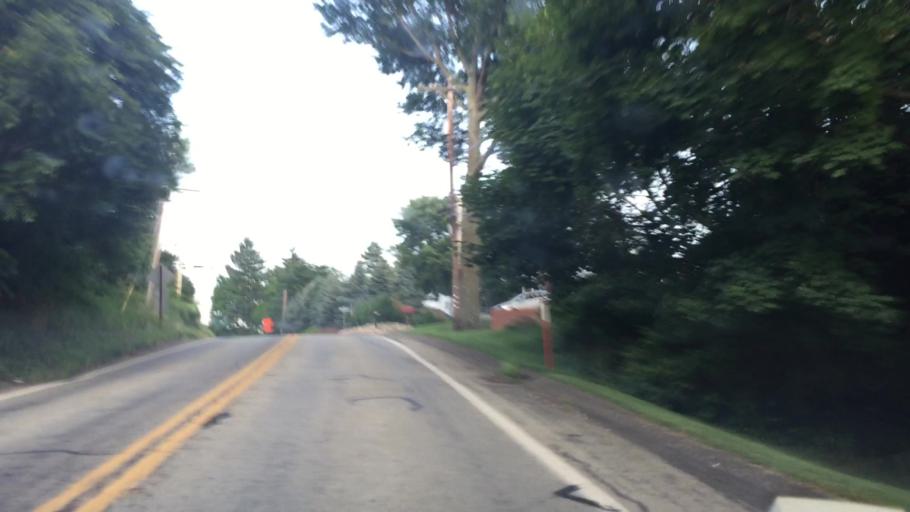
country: US
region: Pennsylvania
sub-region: Allegheny County
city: Glenshaw
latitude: 40.5292
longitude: -79.9993
